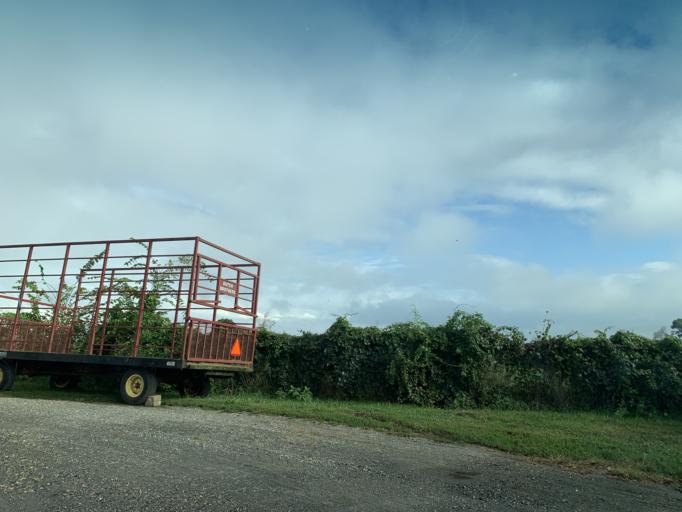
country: US
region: Maryland
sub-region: Harford County
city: Havre de Grace
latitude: 39.5613
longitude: -76.1285
